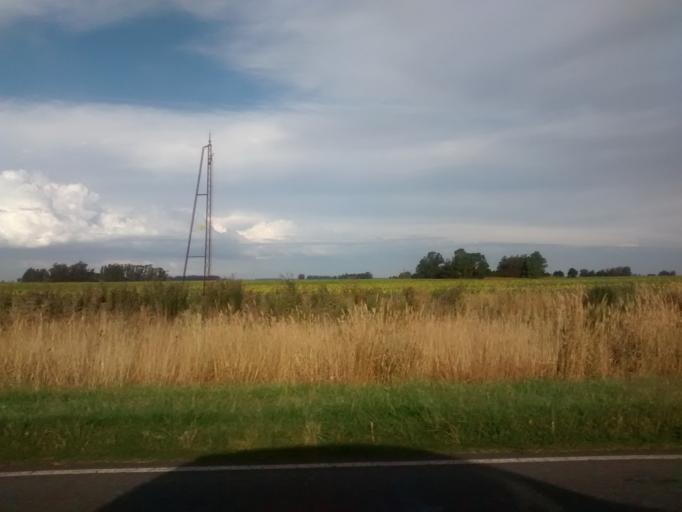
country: AR
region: Buenos Aires
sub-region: Partido de Loberia
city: Loberia
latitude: -38.2125
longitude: -58.7330
